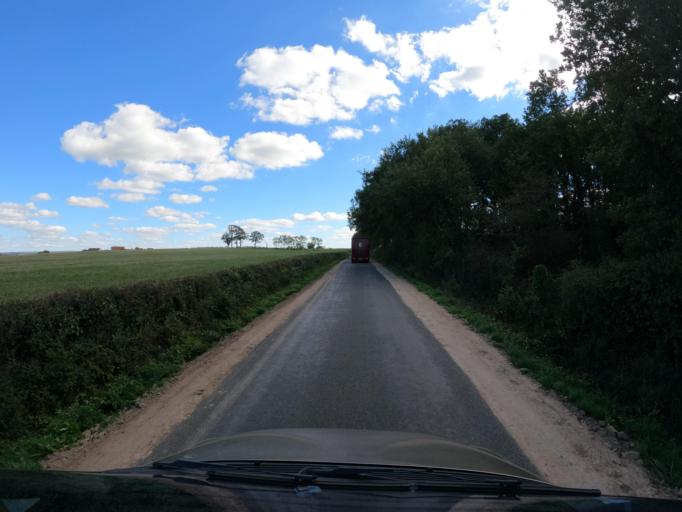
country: FR
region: Auvergne
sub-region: Departement de l'Allier
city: Doyet
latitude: 46.3842
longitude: 2.7738
